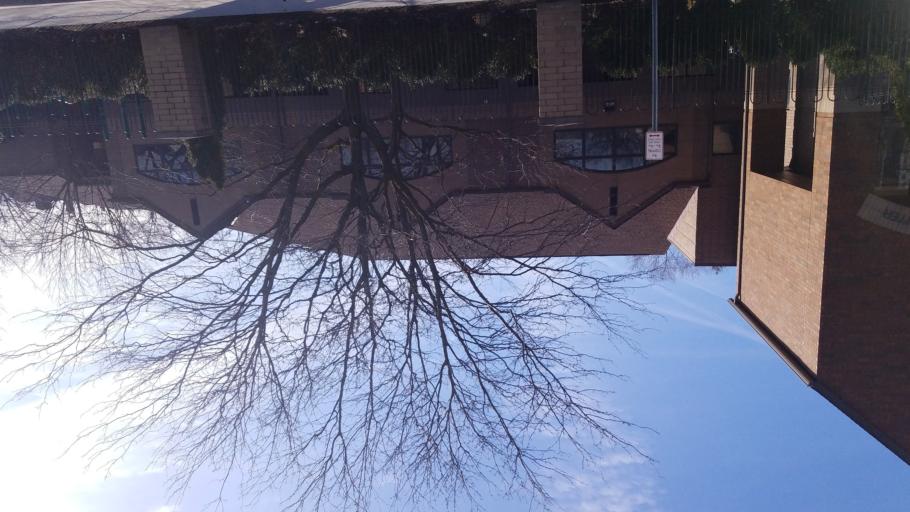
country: US
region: Ohio
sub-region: Franklin County
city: Columbus
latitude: 39.9508
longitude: -82.9766
